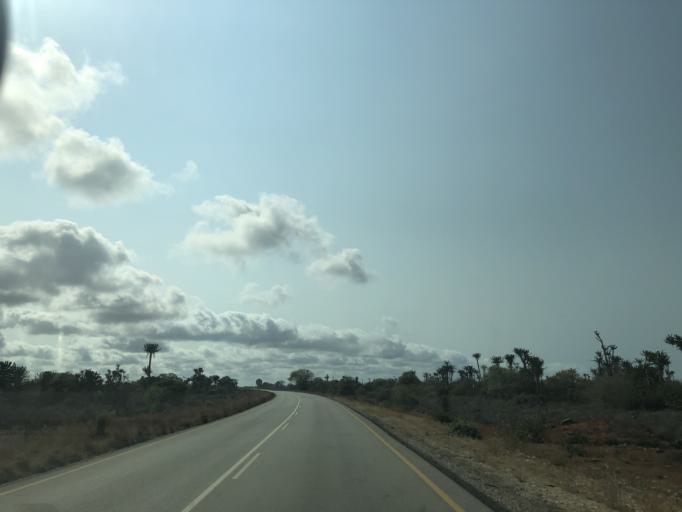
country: AO
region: Luanda
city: Luanda
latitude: -9.7077
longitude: 13.2184
